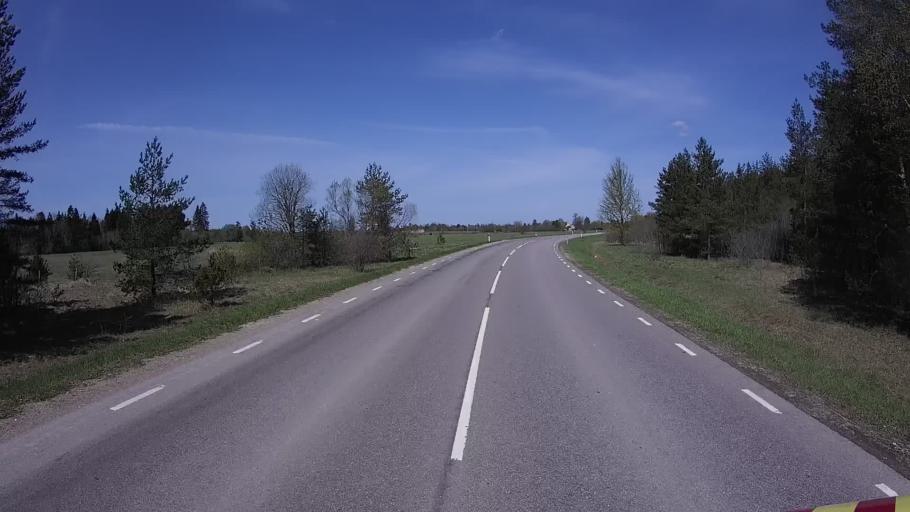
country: EE
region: Harju
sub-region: Keila linn
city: Keila
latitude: 59.2997
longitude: 24.3239
